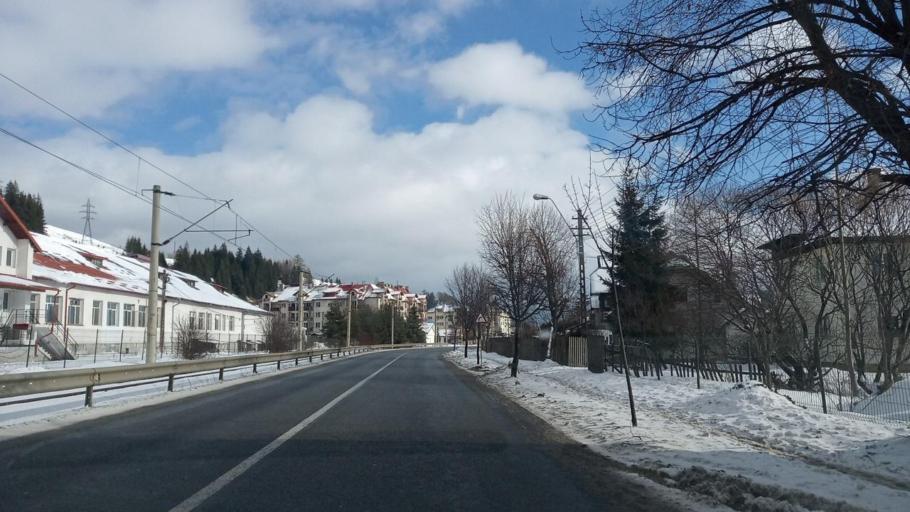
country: RO
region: Suceava
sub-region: Municipiul Vatra Dornei
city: Vatra Dornei
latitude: 47.3487
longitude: 25.3345
